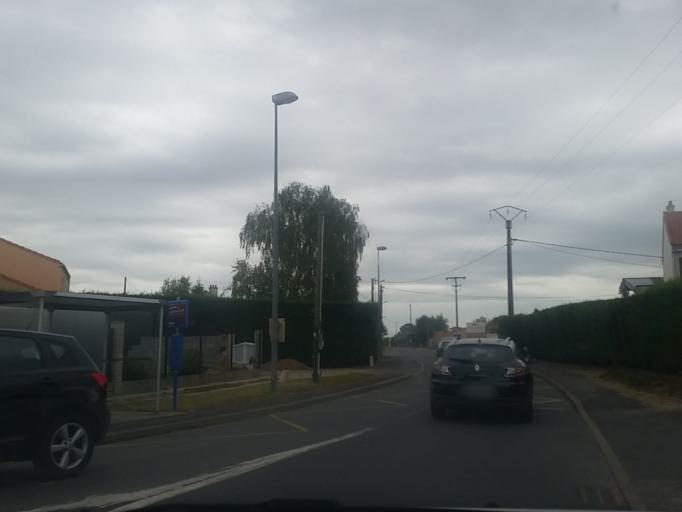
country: FR
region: Pays de la Loire
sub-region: Departement de la Loire-Atlantique
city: La Remaudiere
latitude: 47.2392
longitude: -1.2143
